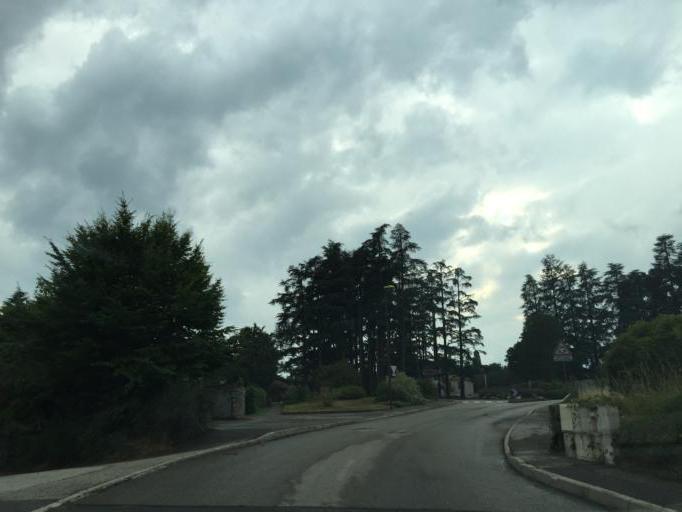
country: FR
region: Rhone-Alpes
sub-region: Departement de la Loire
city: La Talaudiere
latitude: 45.4868
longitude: 4.4371
